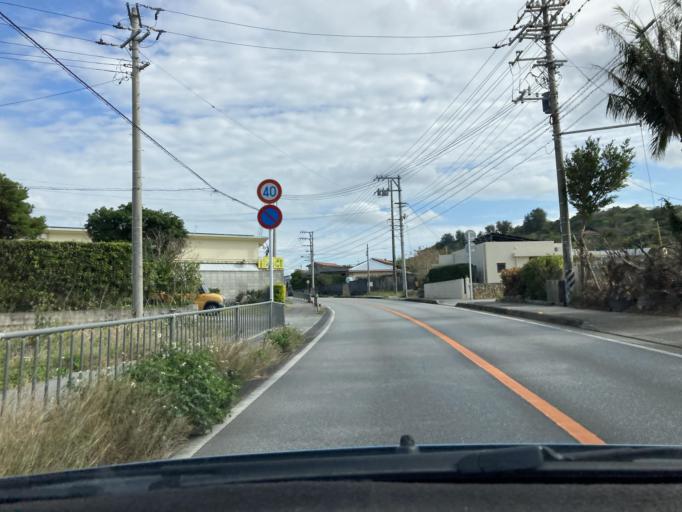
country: JP
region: Okinawa
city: Nago
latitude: 26.6979
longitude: 127.9341
